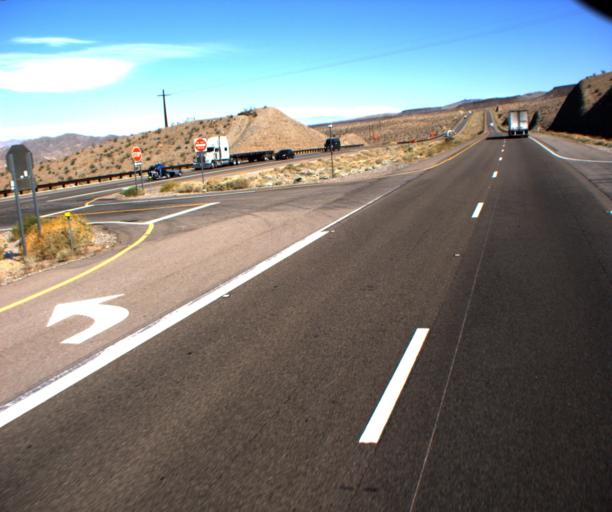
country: US
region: Nevada
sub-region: Clark County
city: Boulder City
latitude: 35.9155
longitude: -114.6294
